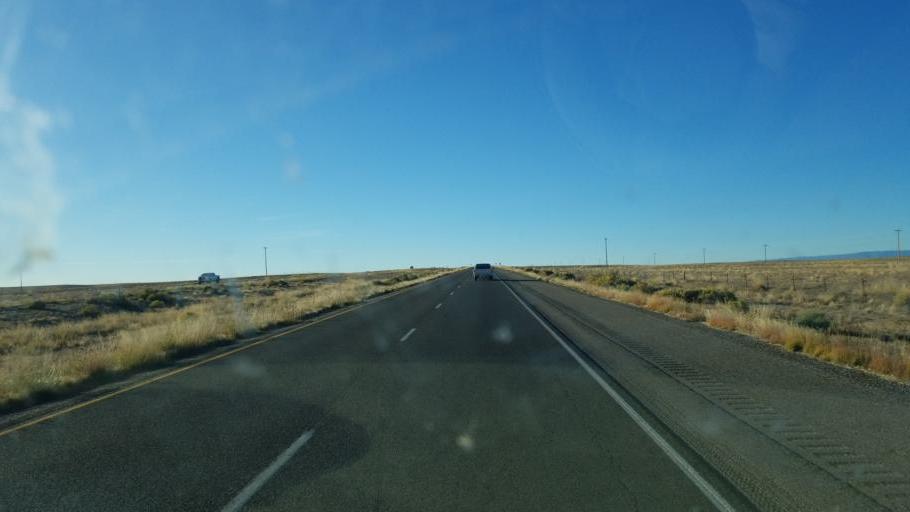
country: US
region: New Mexico
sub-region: San Juan County
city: Shiprock
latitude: 36.6998
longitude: -108.7088
